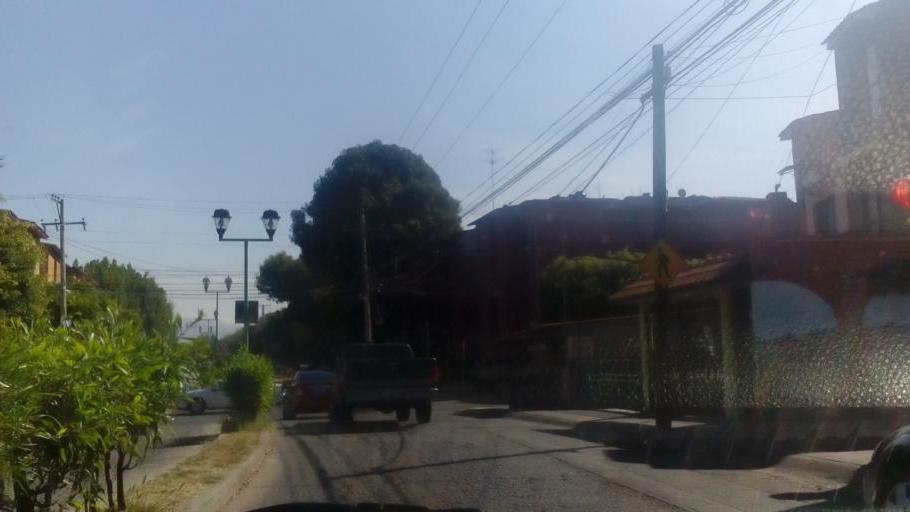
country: MX
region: Guanajuato
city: Leon
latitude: 21.1566
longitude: -101.6829
